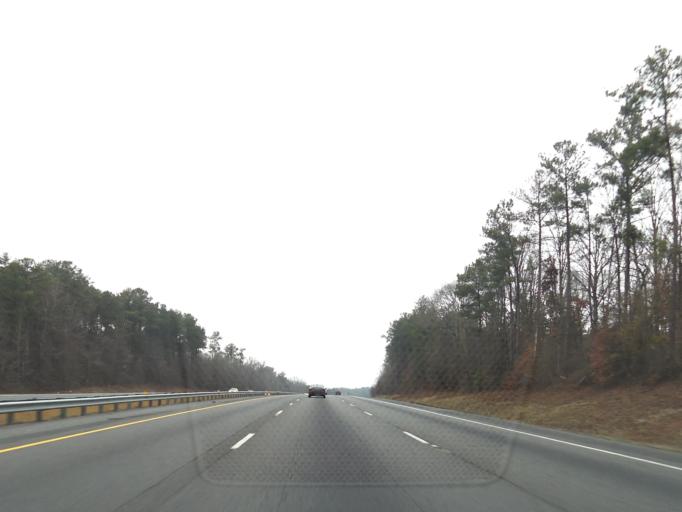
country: US
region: Georgia
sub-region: Henry County
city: Locust Grove
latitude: 33.3199
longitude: -84.1199
